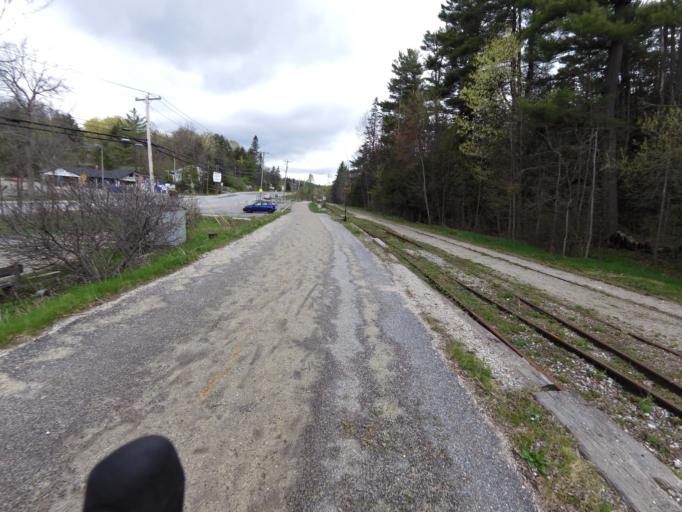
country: CA
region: Quebec
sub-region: Outaouais
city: Wakefield
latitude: 45.6418
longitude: -75.9273
